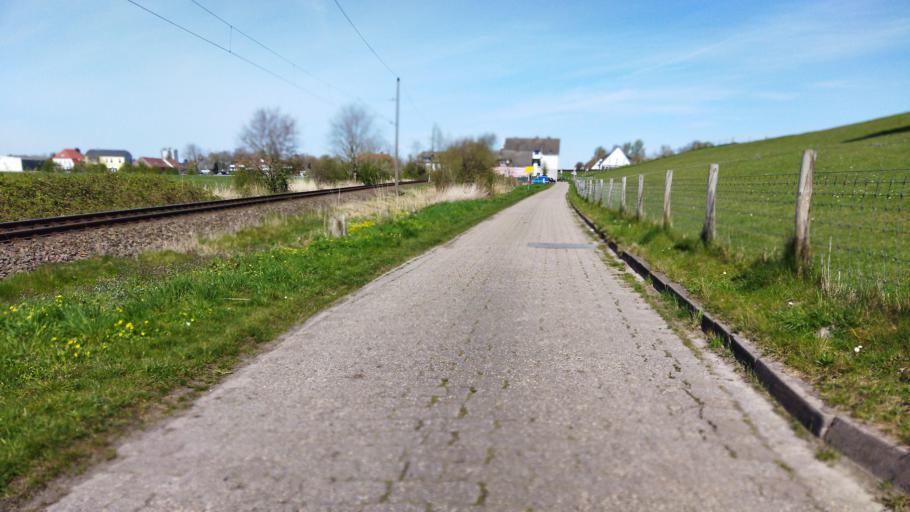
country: DE
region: Lower Saxony
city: Nordenham
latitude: 53.4651
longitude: 8.4758
